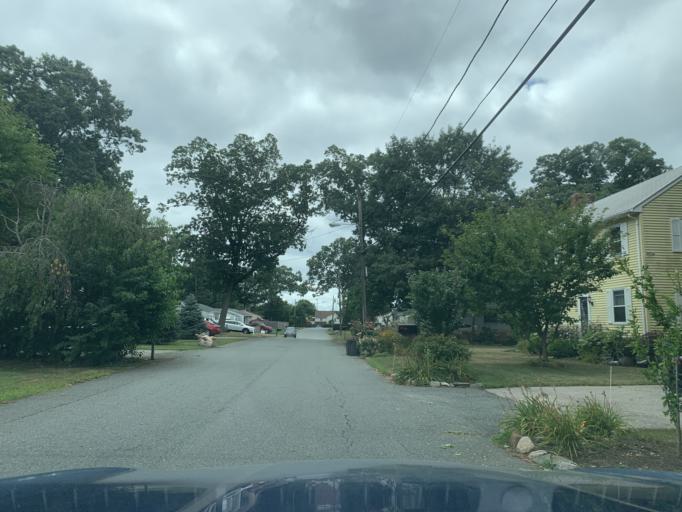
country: US
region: Rhode Island
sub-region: Kent County
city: Warwick
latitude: 41.7228
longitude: -71.4638
